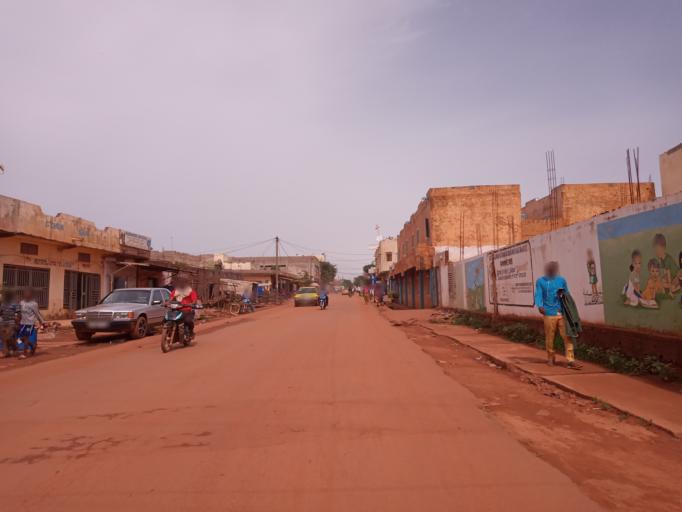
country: ML
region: Bamako
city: Bamako
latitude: 12.5537
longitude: -7.9928
